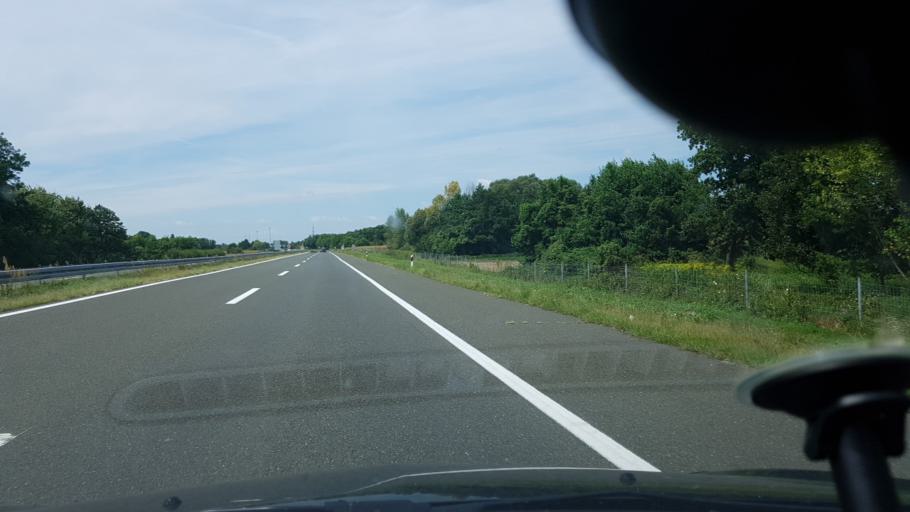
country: HR
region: Medimurska
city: Hodosan
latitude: 46.4112
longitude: 16.6537
